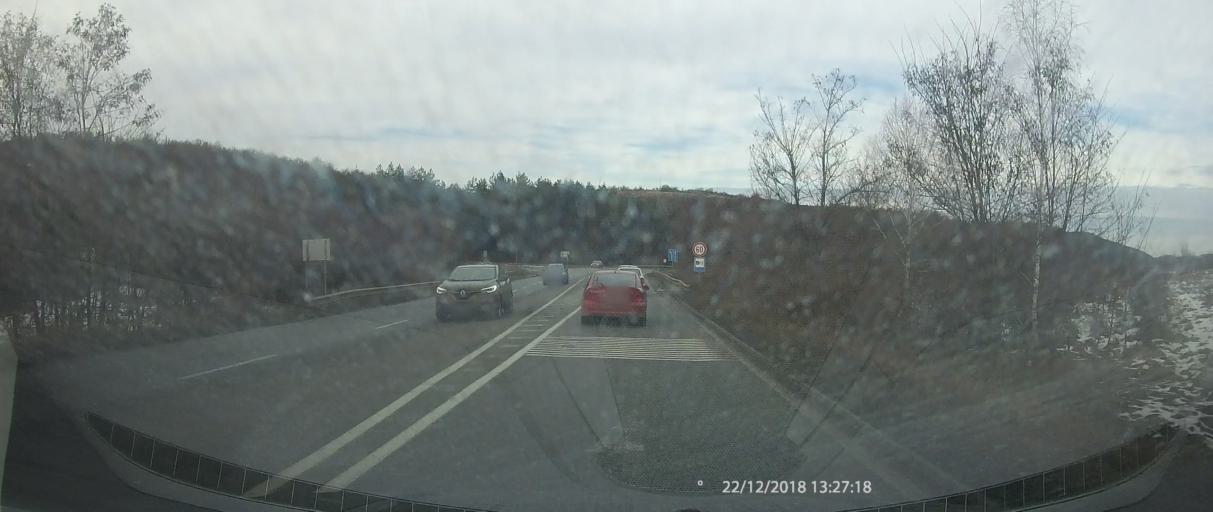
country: BG
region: Lovech
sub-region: Obshtina Yablanitsa
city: Yablanitsa
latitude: 43.0542
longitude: 24.1321
